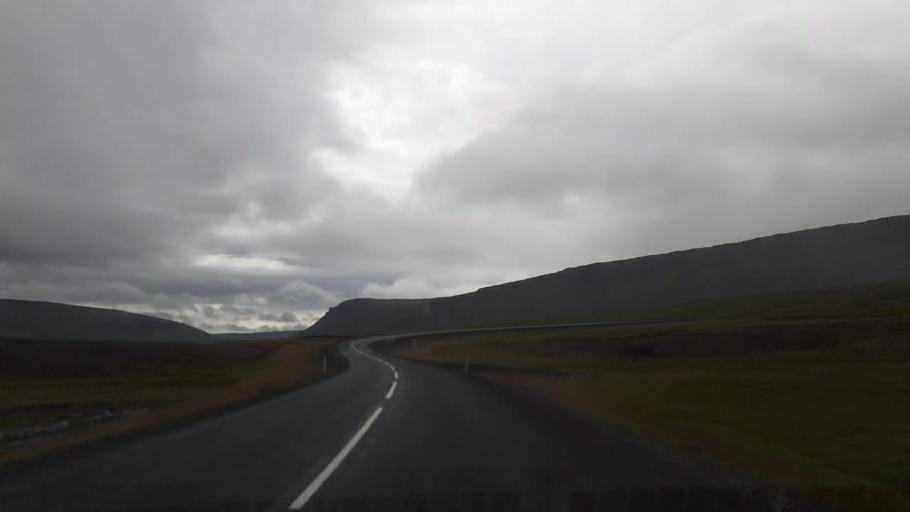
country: IS
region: East
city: Egilsstadir
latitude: 65.6268
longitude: -15.0715
